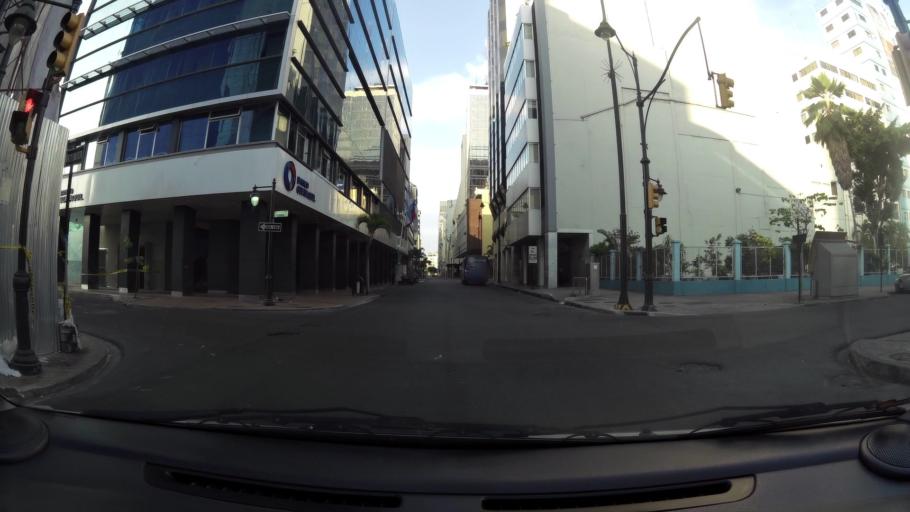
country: EC
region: Guayas
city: Eloy Alfaro
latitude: -2.1908
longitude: -79.8800
